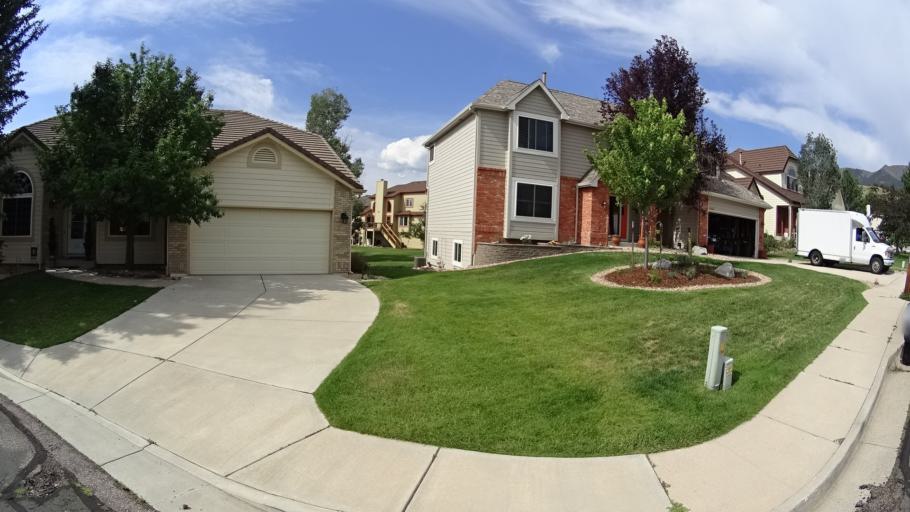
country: US
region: Colorado
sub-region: El Paso County
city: Air Force Academy
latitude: 38.9504
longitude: -104.8664
